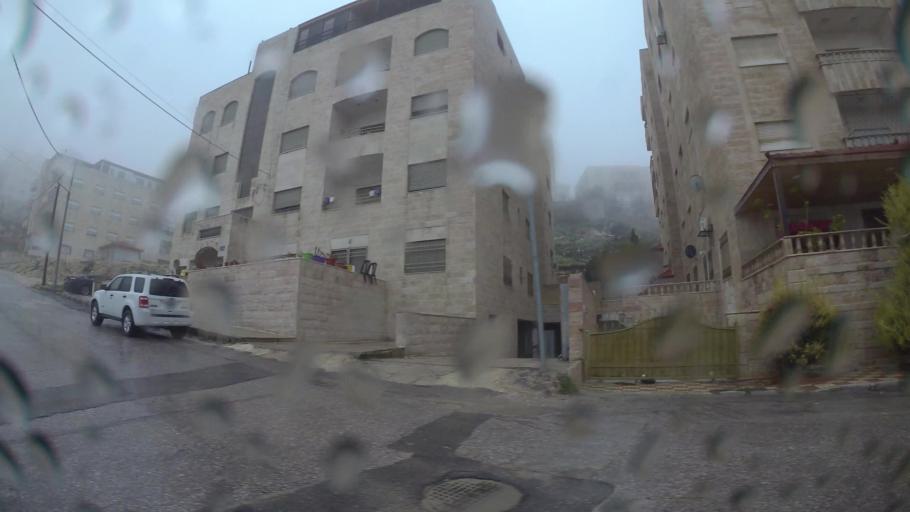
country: JO
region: Amman
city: Al Jubayhah
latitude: 32.0093
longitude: 35.8868
